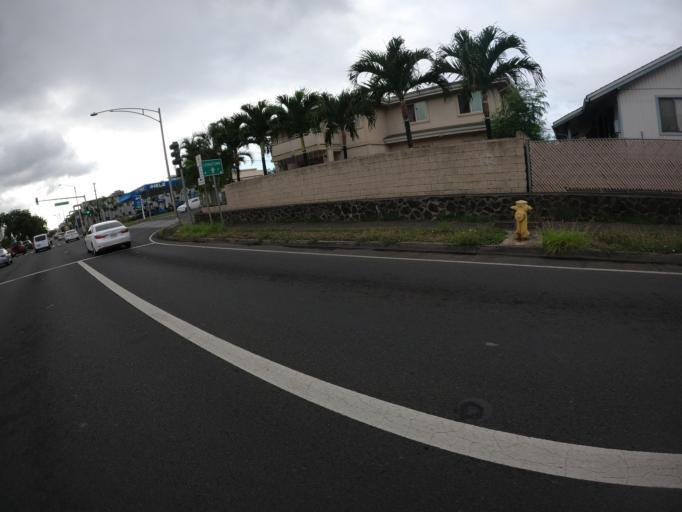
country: US
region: Hawaii
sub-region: Honolulu County
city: Honolulu
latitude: 21.3237
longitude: -157.8651
